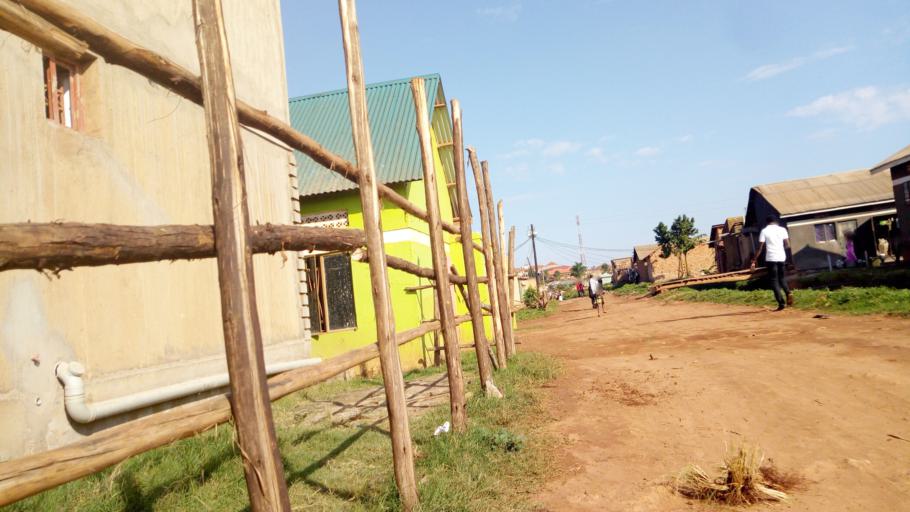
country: UG
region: Central Region
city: Kampala Central Division
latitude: 0.3437
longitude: 32.5573
